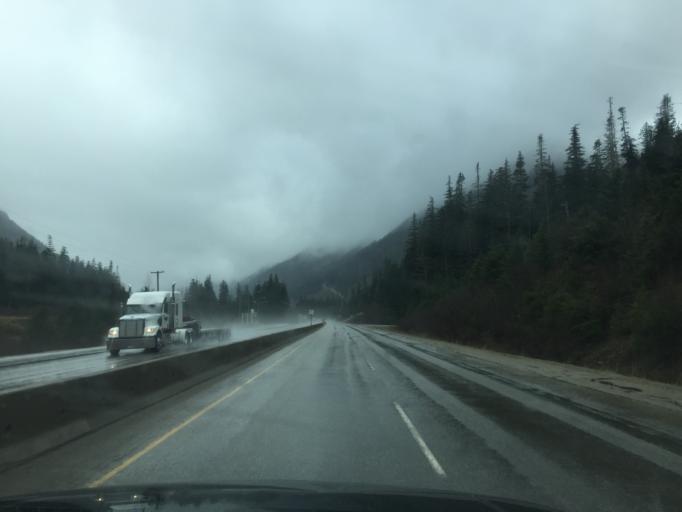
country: CA
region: British Columbia
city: Hope
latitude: 49.5793
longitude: -121.1756
